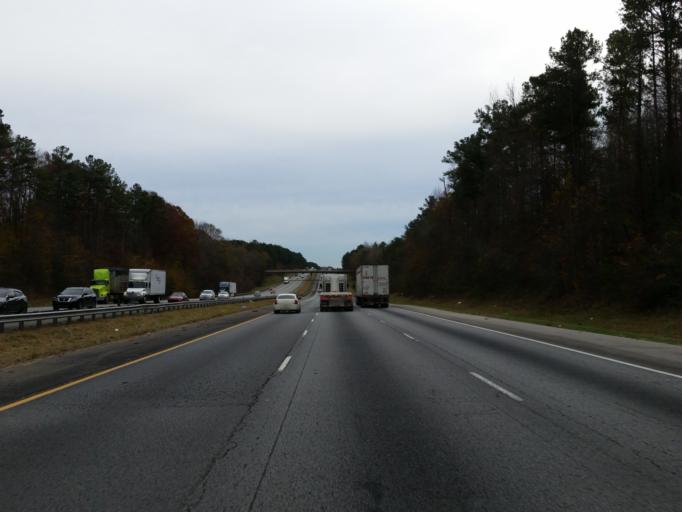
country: US
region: Georgia
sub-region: Henry County
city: Locust Grove
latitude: 33.3188
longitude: -84.1197
